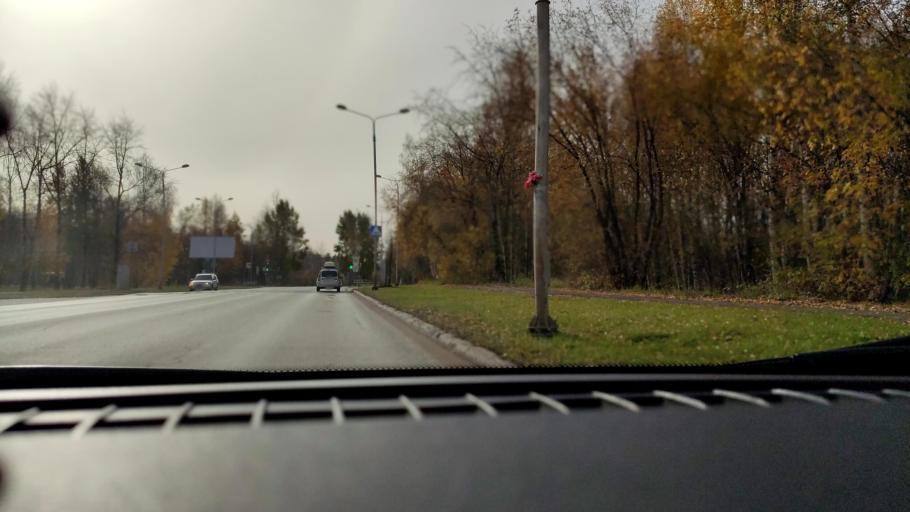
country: RU
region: Perm
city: Perm
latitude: 58.0925
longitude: 56.3831
